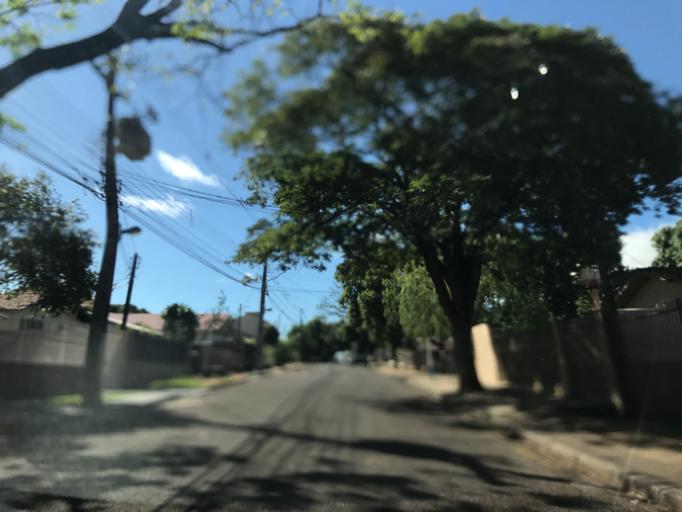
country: BR
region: Parana
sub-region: Maringa
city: Maringa
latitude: -23.4522
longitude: -51.9595
